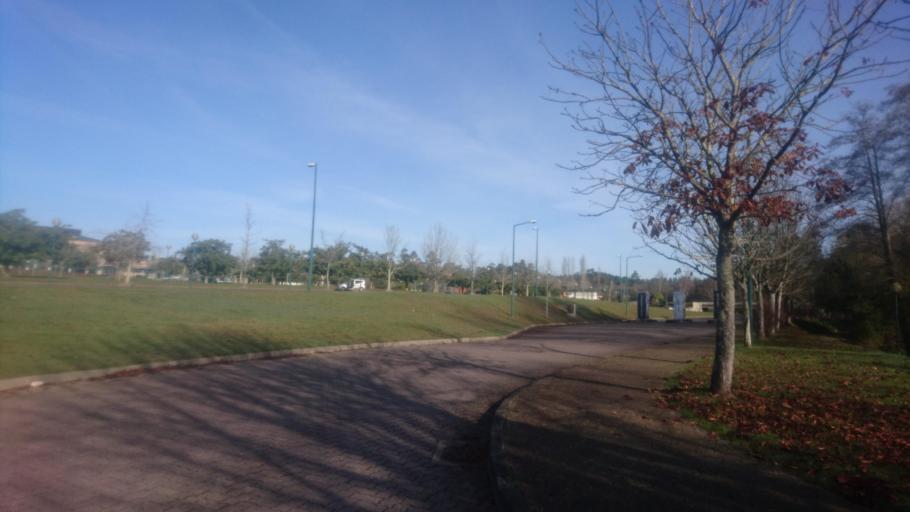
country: PT
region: Aveiro
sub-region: Santa Maria da Feira
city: Rio Meao
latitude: 40.9321
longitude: -8.5768
